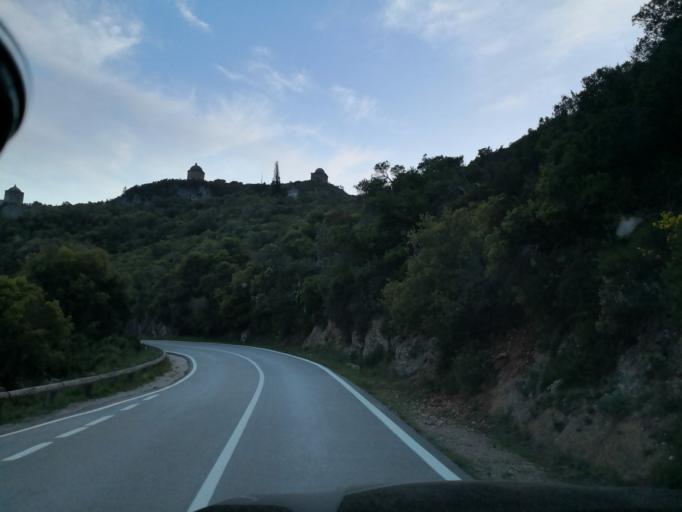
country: PT
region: Setubal
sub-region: Palmela
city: Quinta do Anjo
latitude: 38.4741
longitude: -8.9961
